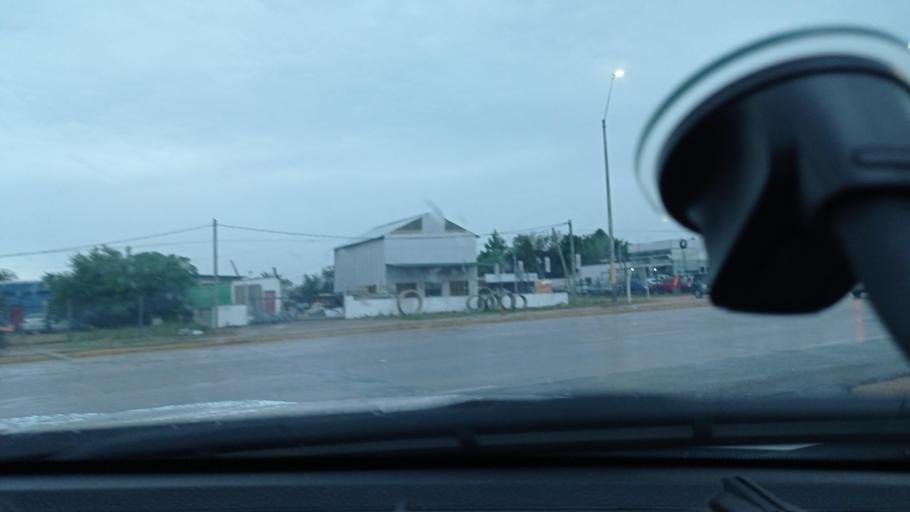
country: UY
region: Canelones
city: Joaquin Suarez
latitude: -34.7595
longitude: -56.0120
